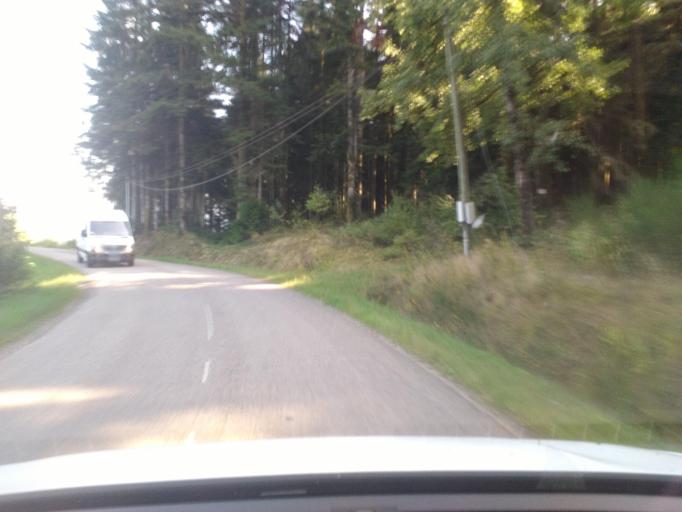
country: FR
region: Lorraine
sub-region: Departement des Vosges
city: Ban-de-Laveline
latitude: 48.3182
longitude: 7.0764
